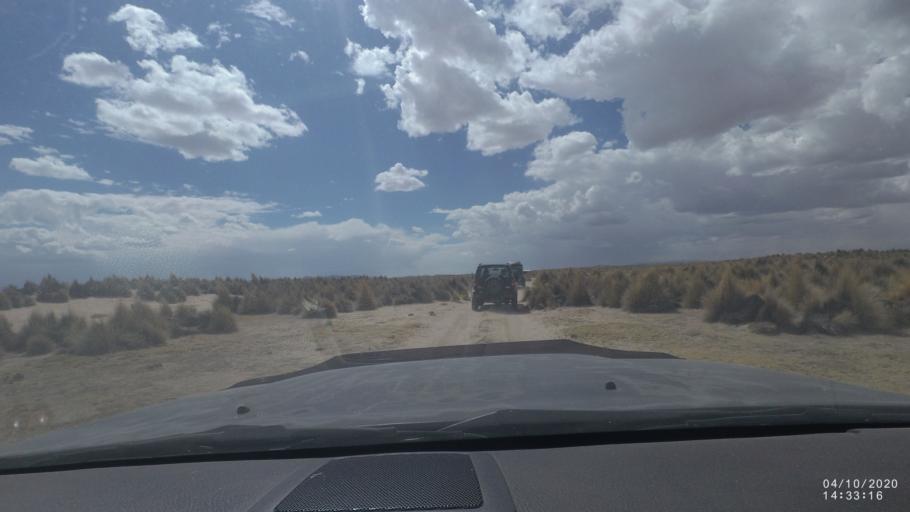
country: BO
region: Oruro
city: Poopo
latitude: -18.6718
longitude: -67.4667
